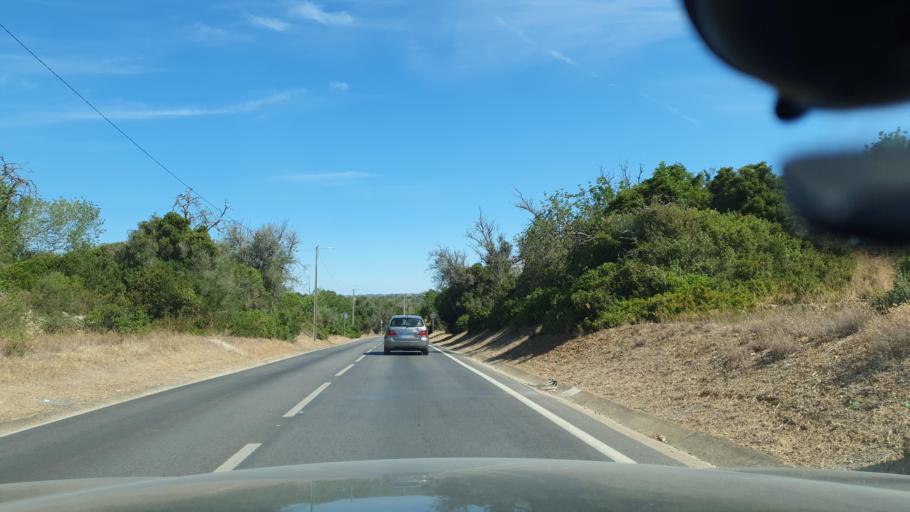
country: PT
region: Faro
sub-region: Albufeira
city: Guia
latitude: 37.1039
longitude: -8.3079
